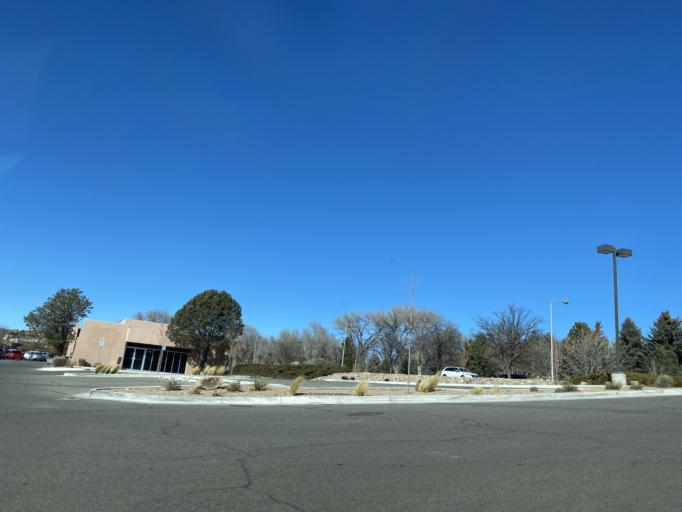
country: US
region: New Mexico
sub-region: Santa Fe County
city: Santa Fe
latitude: 35.6932
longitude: -105.9492
